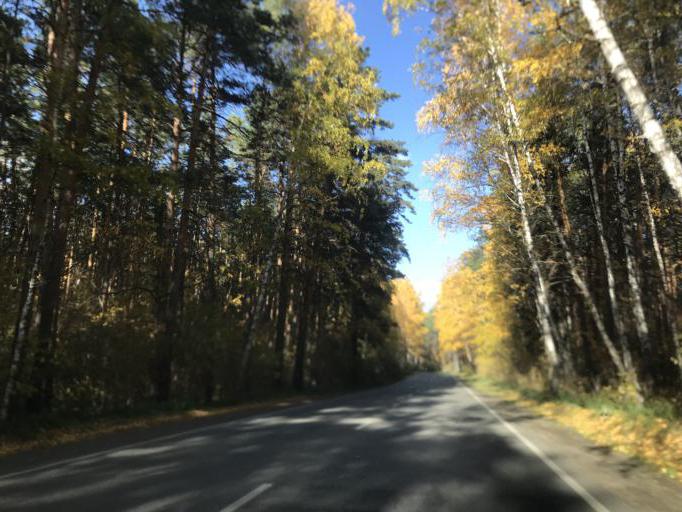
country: RU
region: Chelyabinsk
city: Dolgoderevenskoye
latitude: 55.2922
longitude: 61.3569
